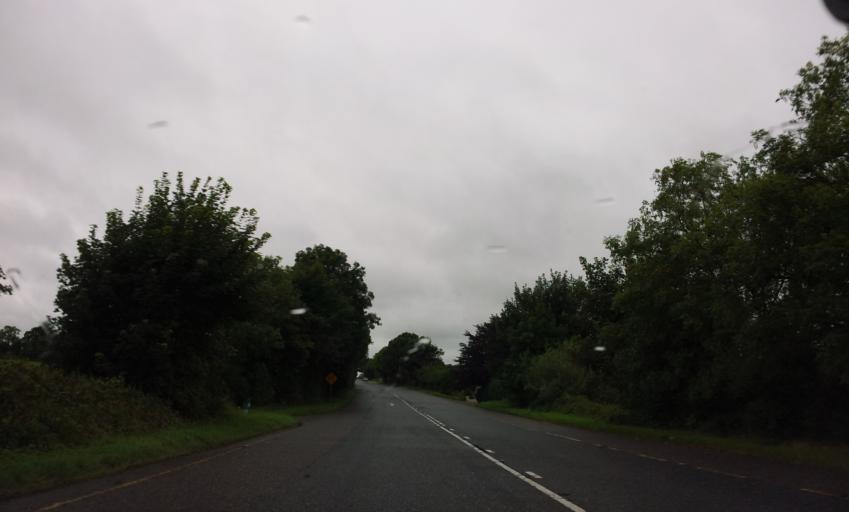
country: IE
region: Munster
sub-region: County Cork
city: Mitchelstown
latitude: 52.2849
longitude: -8.2288
